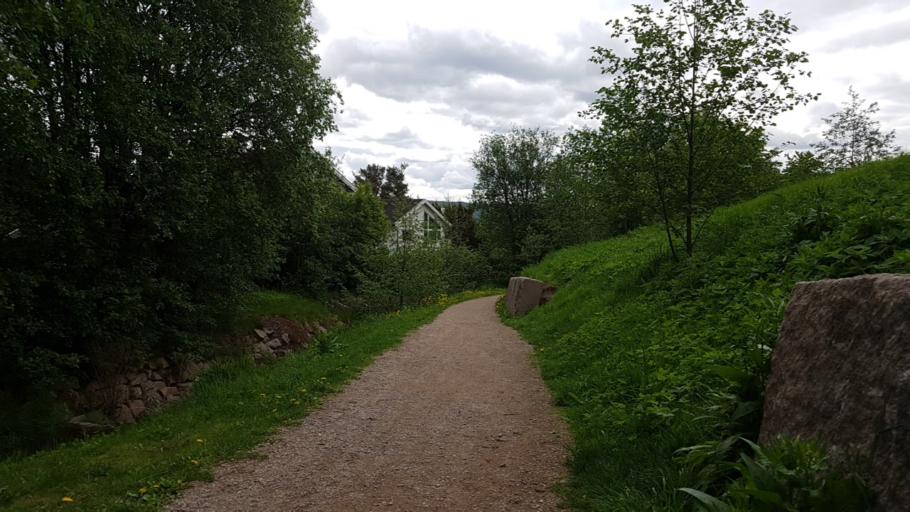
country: NO
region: Oslo
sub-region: Oslo
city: Oslo
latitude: 59.9433
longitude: 10.8190
